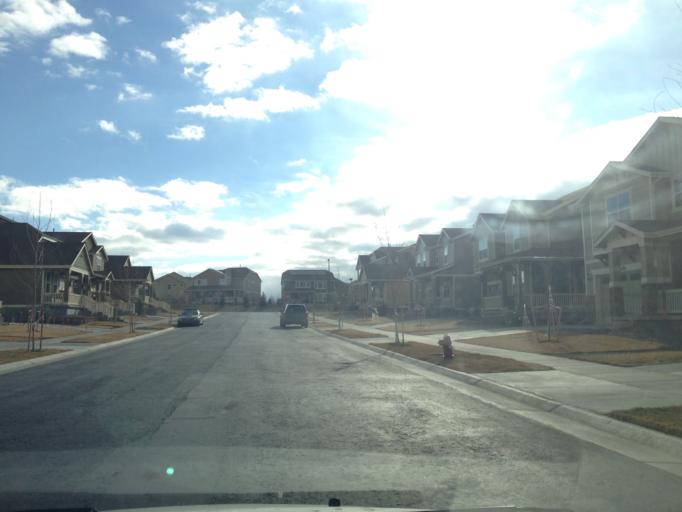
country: US
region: Colorado
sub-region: Boulder County
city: Erie
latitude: 40.0353
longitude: -105.0868
